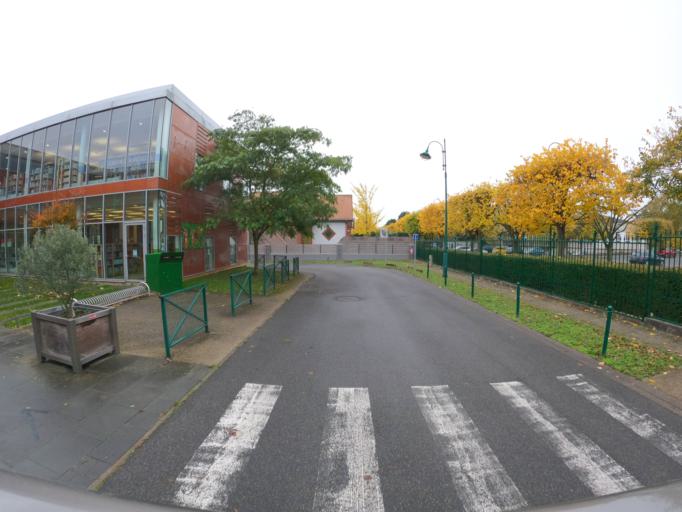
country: FR
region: Ile-de-France
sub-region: Departement du Val-de-Marne
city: Ormesson-sur-Marne
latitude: 48.7874
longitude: 2.5453
